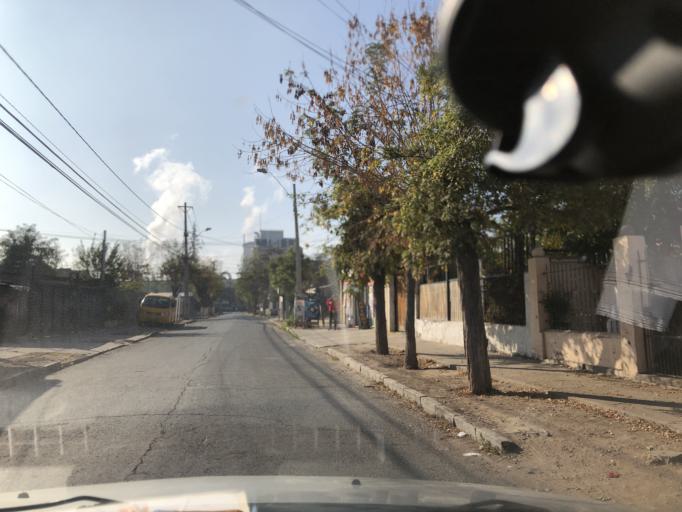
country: CL
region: Santiago Metropolitan
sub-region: Provincia de Cordillera
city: Puente Alto
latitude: -33.6212
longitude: -70.5758
